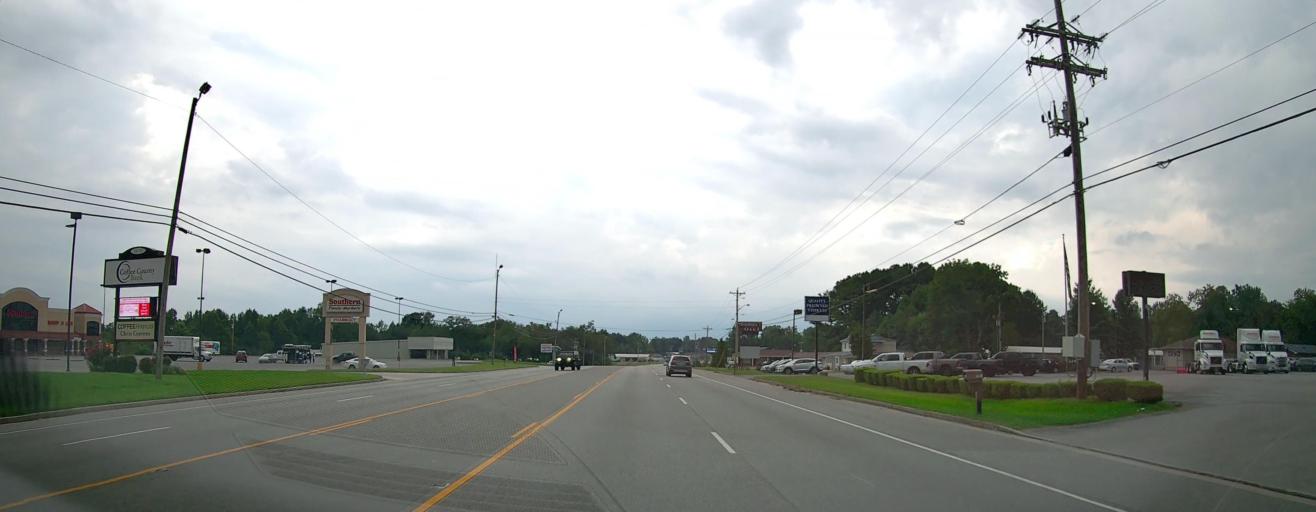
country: US
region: Tennessee
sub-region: Coffee County
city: Manchester
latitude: 35.4607
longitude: -86.0606
